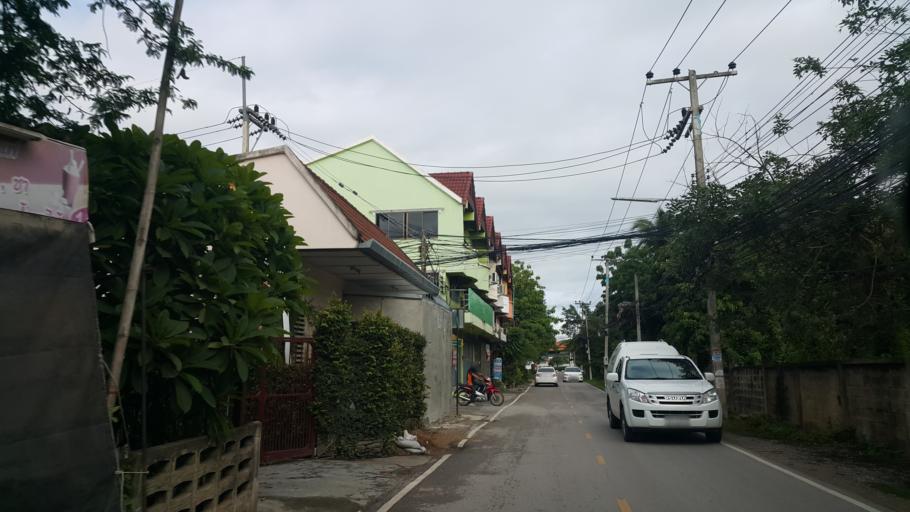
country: TH
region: Chiang Mai
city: Chiang Mai
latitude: 18.7483
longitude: 98.9651
